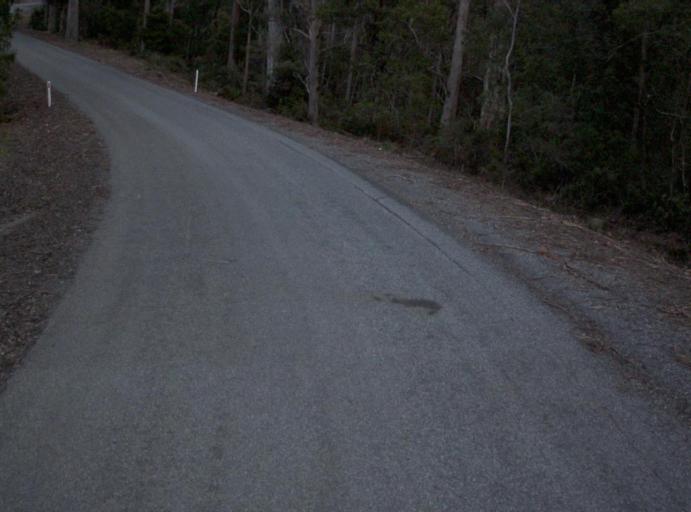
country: AU
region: Tasmania
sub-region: Launceston
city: Newstead
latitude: -41.3104
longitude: 147.3333
